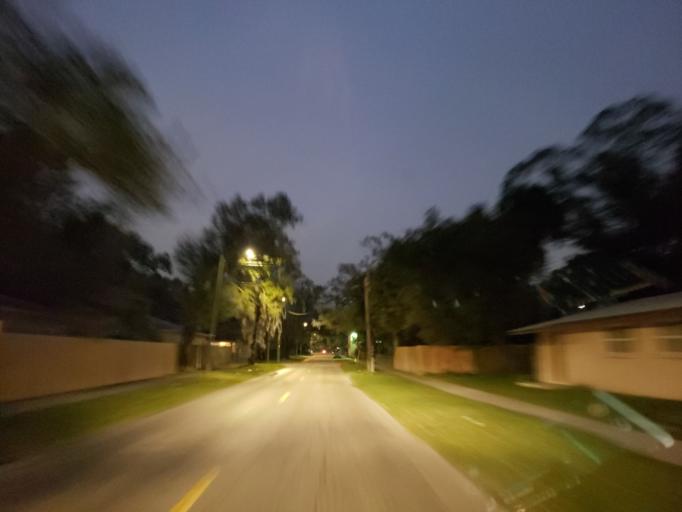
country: US
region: Florida
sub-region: Hillsborough County
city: University
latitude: 28.0226
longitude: -82.4488
